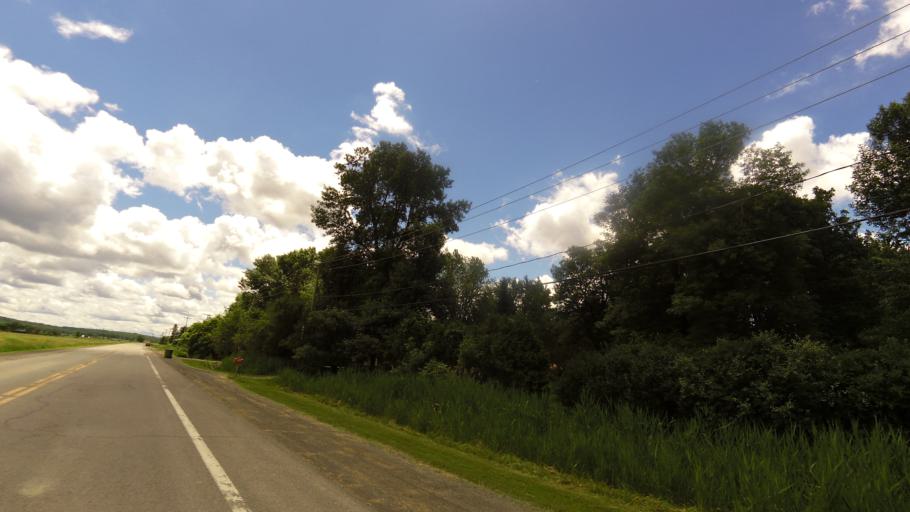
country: CA
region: Quebec
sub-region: Monteregie
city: Hudson
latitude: 45.5262
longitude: -74.1739
